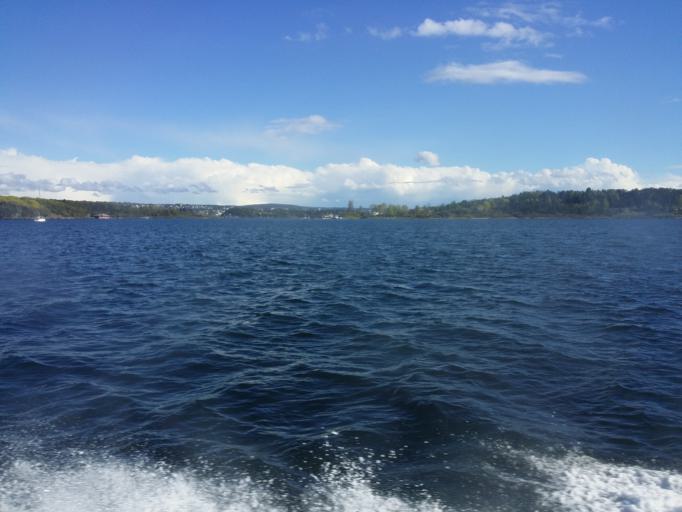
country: NO
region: Oslo
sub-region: Oslo
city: Oslo
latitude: 59.8996
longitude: 10.7115
